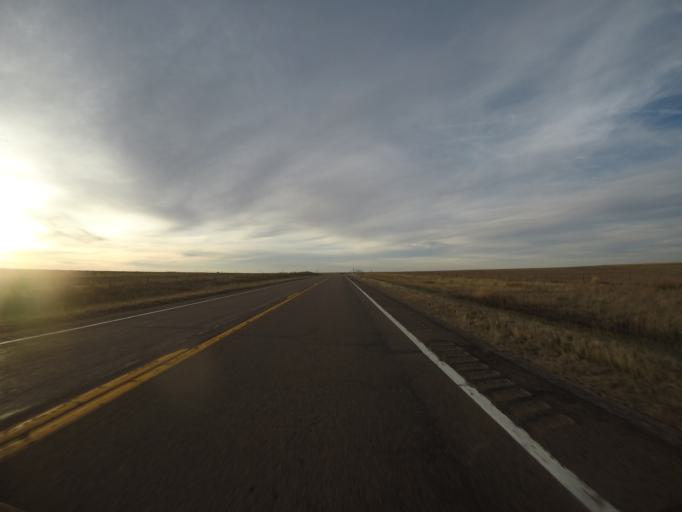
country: US
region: Colorado
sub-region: Washington County
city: Akron
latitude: 39.7355
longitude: -103.1714
